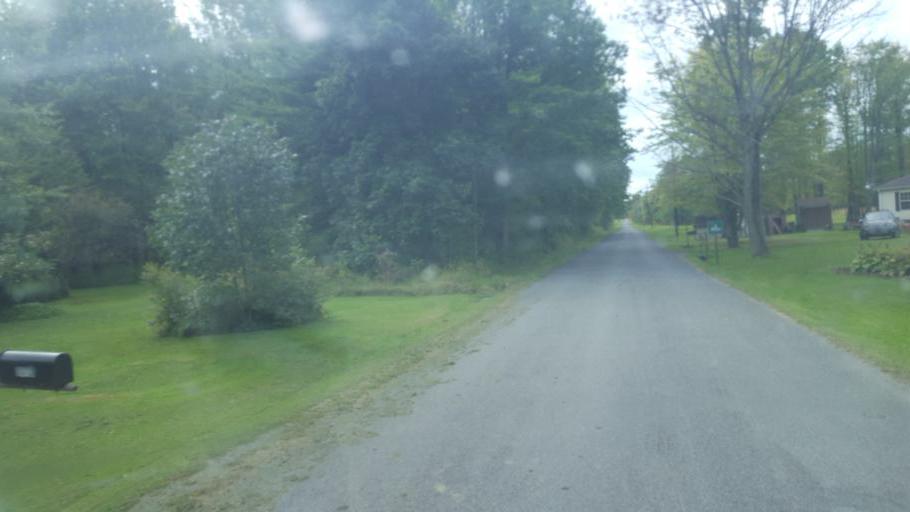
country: US
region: Pennsylvania
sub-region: Crawford County
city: Pymatuning Central
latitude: 41.5387
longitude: -80.4160
